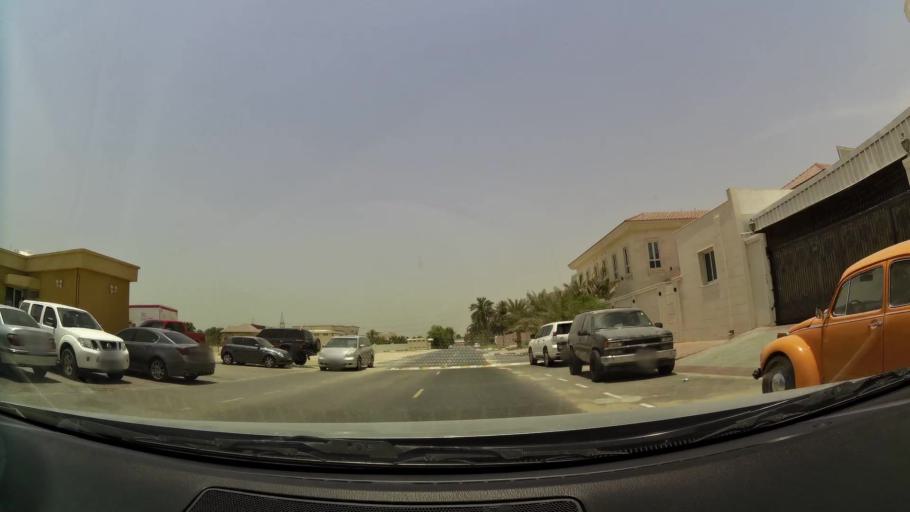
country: AE
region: Ash Shariqah
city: Sharjah
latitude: 25.2101
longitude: 55.3834
